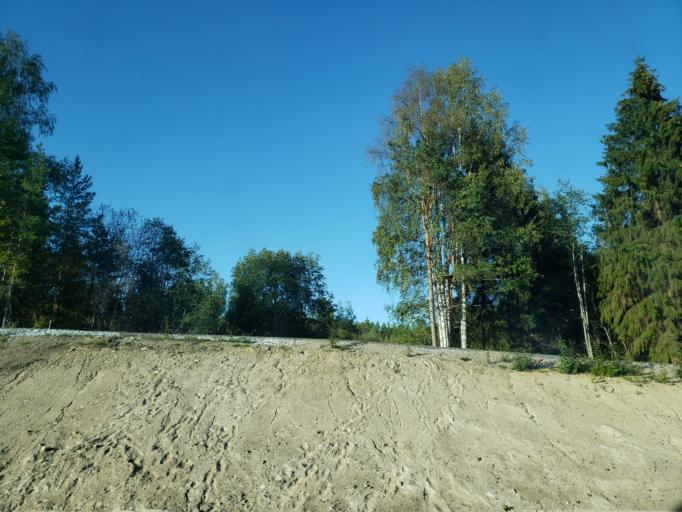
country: FI
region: South Karelia
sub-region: Lappeenranta
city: Nuijamaa
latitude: 60.8567
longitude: 28.3338
